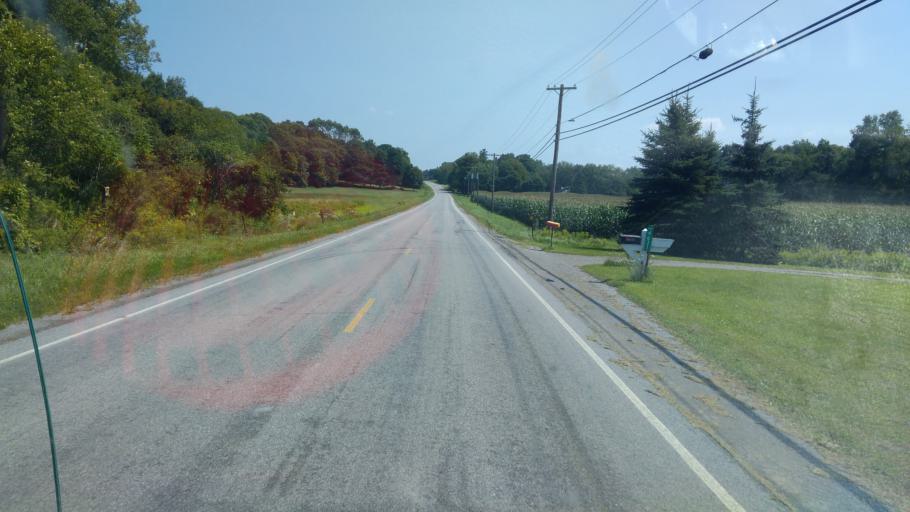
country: US
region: New York
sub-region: Allegany County
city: Belmont
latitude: 42.3019
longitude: -77.9941
